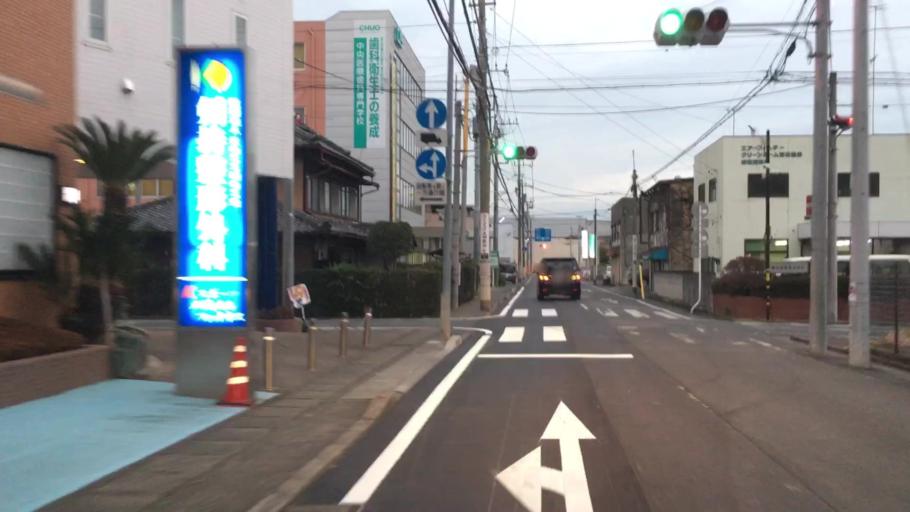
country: JP
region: Gunma
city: Ota
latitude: 36.2982
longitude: 139.3786
